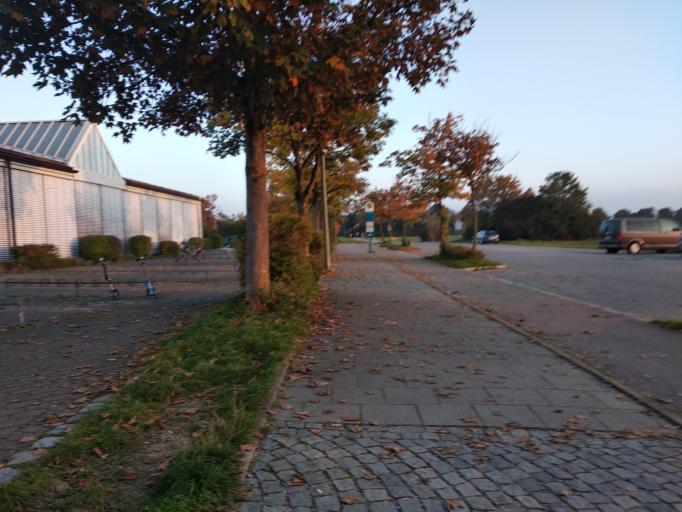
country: DE
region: Bavaria
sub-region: Upper Bavaria
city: Kirchheim bei Muenchen
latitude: 48.1673
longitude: 11.7588
